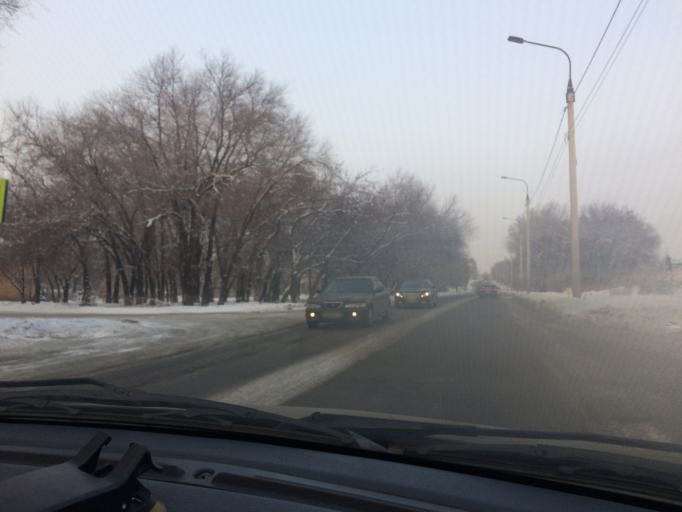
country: RU
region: Chelyabinsk
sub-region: Gorod Magnitogorsk
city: Magnitogorsk
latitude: 53.4668
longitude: 59.0732
